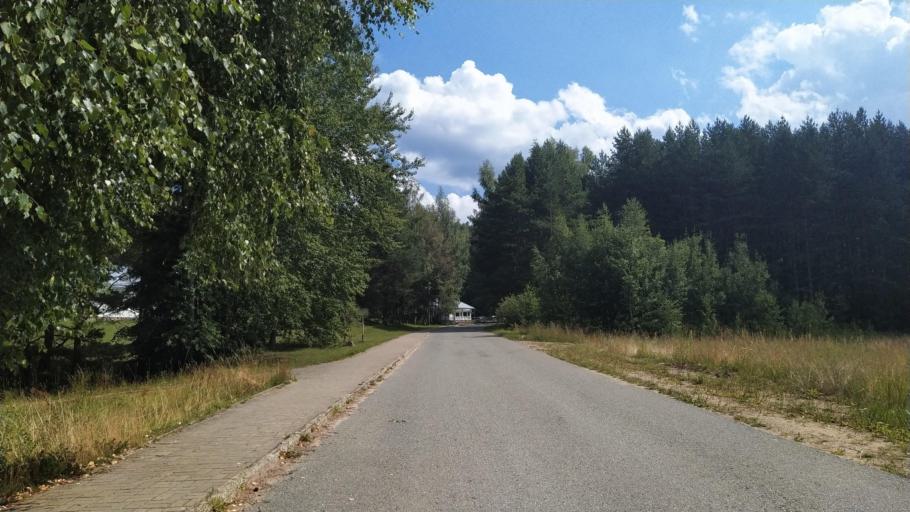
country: RU
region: Pskov
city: Pushkinskiye Gory
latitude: 57.0765
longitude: 28.9546
